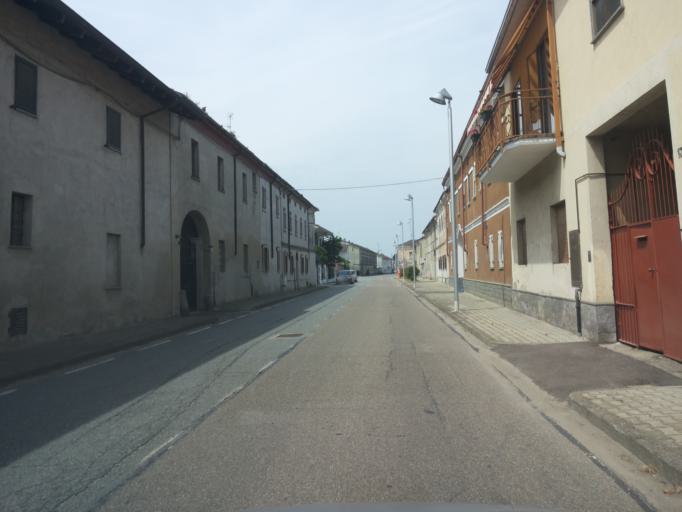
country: IT
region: Piedmont
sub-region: Provincia di Vercelli
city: Pezzana
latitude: 45.2611
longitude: 8.4802
